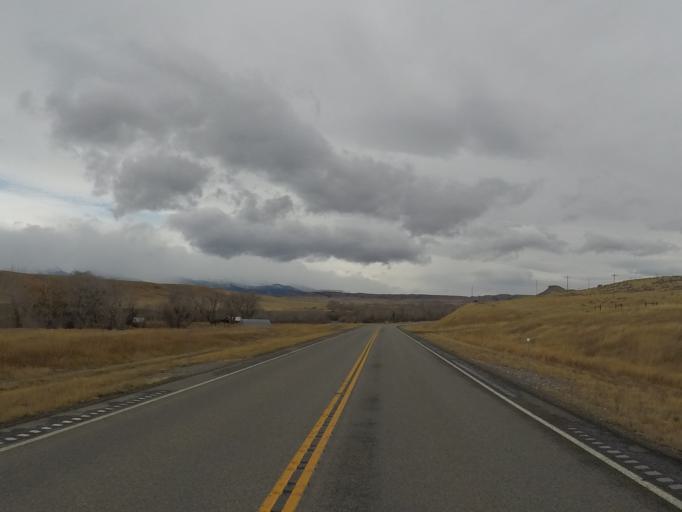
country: US
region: Montana
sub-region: Sweet Grass County
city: Big Timber
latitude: 45.9263
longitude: -109.9827
